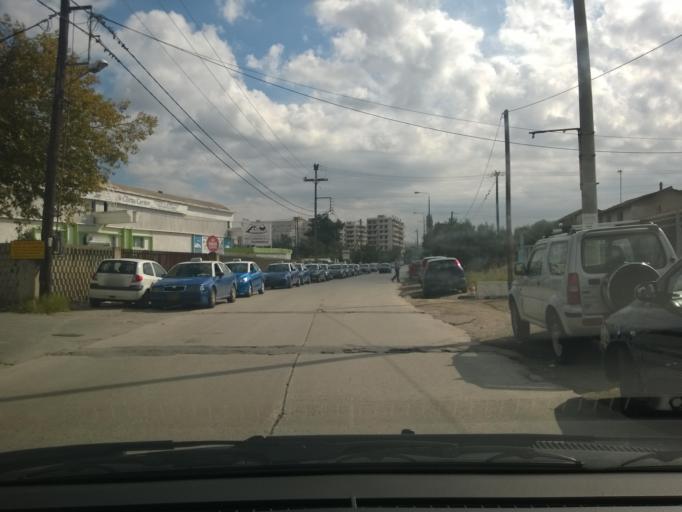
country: GR
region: Central Macedonia
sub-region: Nomos Thessalonikis
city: Menemeni
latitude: 40.6537
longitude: 22.9035
